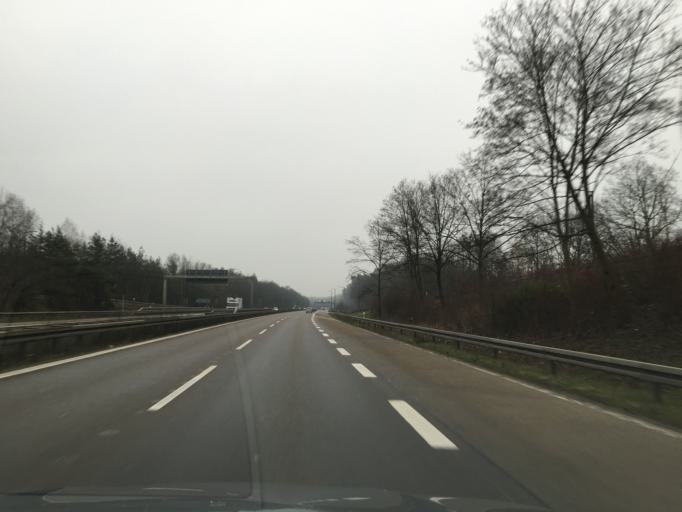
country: DE
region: Bavaria
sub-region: Regierungsbezirk Mittelfranken
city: Nuernberg
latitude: 49.4074
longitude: 11.0709
